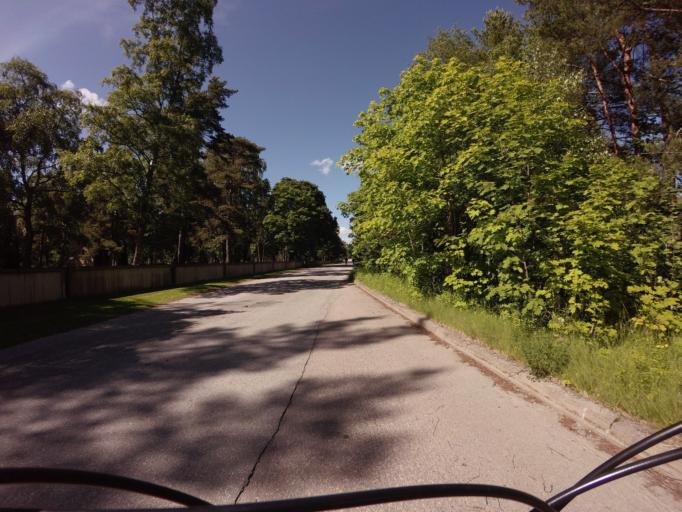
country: FI
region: Varsinais-Suomi
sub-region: Turku
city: Turku
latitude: 60.4914
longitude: 22.2804
